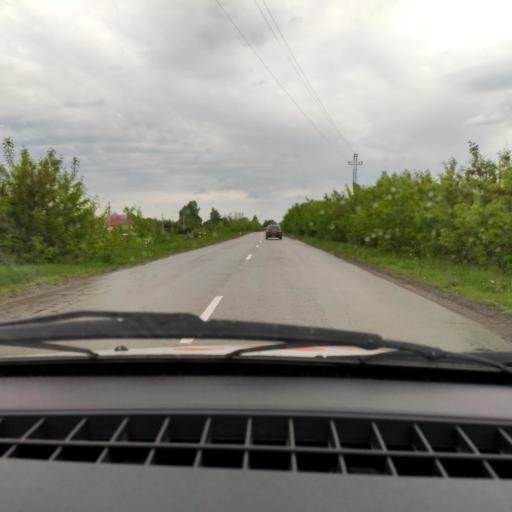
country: RU
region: Bashkortostan
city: Kudeyevskiy
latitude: 54.8295
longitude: 56.7931
